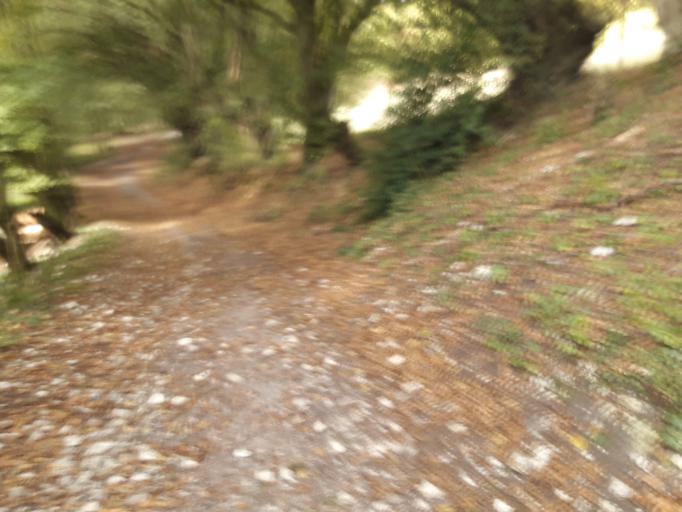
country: DE
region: North Rhine-Westphalia
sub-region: Regierungsbezirk Detmold
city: Schlangen
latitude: 51.8306
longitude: 8.8716
